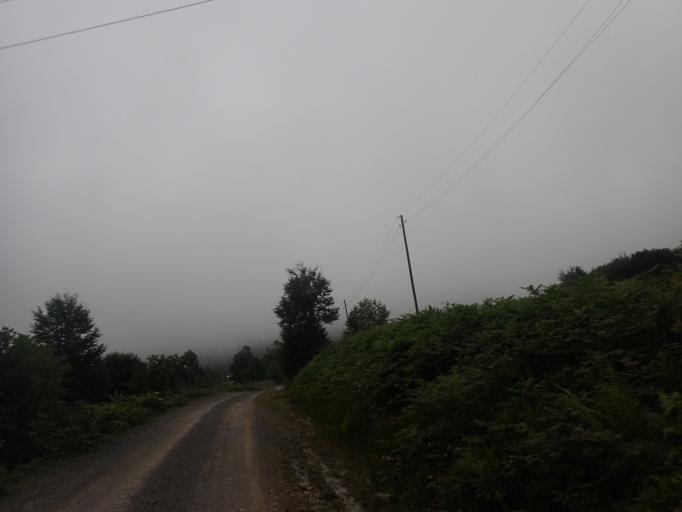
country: TR
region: Ordu
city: Akkus
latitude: 40.8573
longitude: 37.0106
